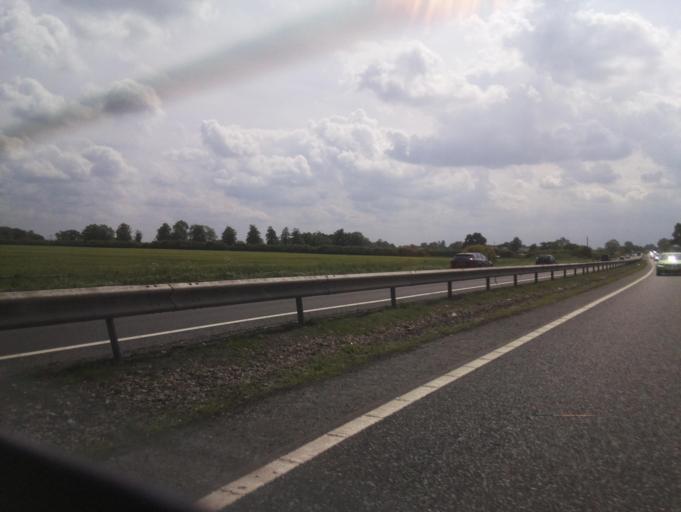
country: GB
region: England
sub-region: North Yorkshire
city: Thirsk
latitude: 54.2691
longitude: -1.3455
